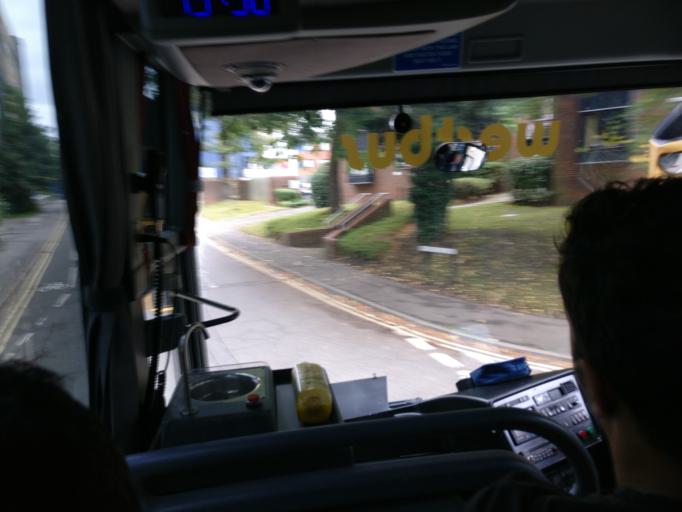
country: GB
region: England
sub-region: Surrey
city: Woking
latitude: 51.3172
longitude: -0.5581
